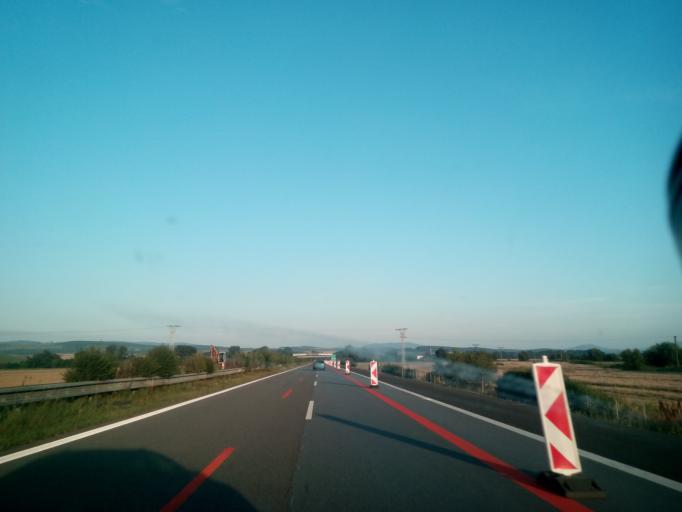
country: SK
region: Kosicky
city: Kosice
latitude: 48.8517
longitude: 21.2793
